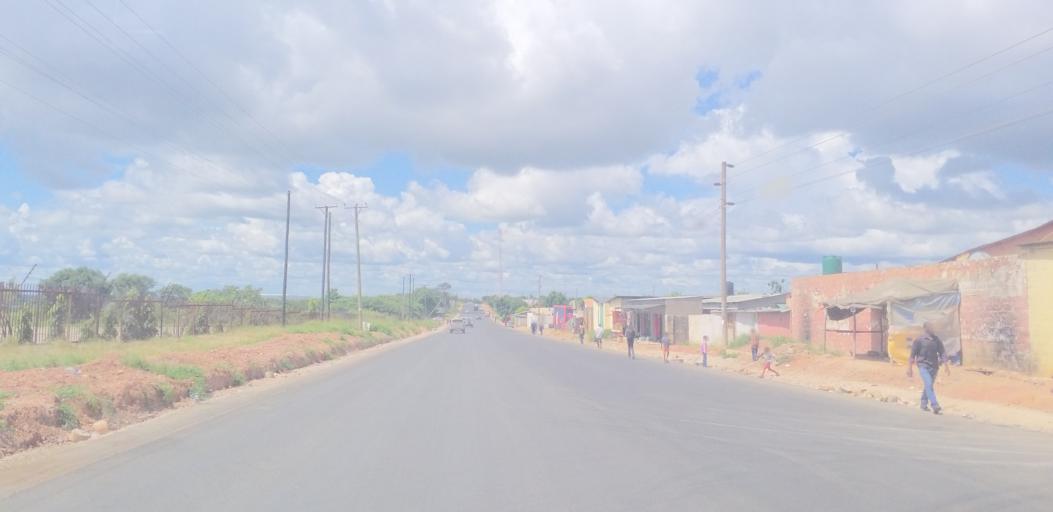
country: ZM
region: Lusaka
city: Lusaka
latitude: -15.3643
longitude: 28.3209
